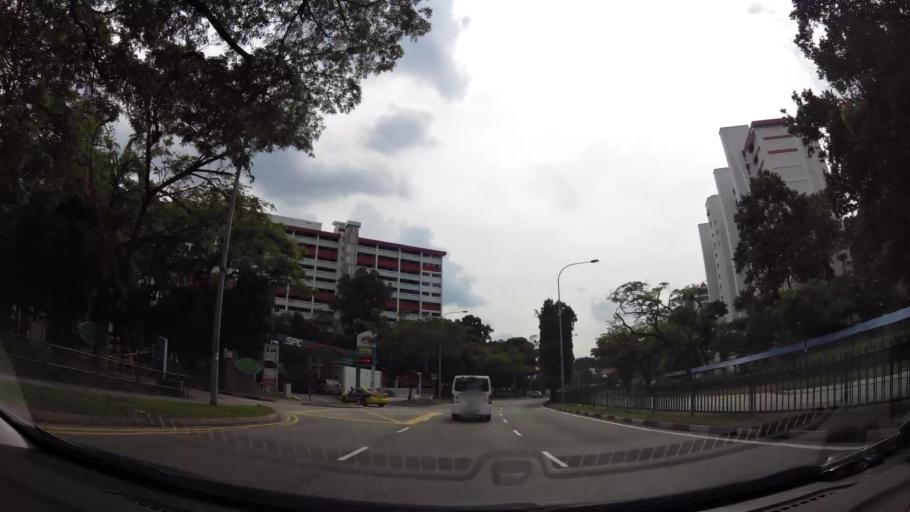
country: MY
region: Johor
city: Johor Bahru
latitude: 1.4429
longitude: 103.7763
